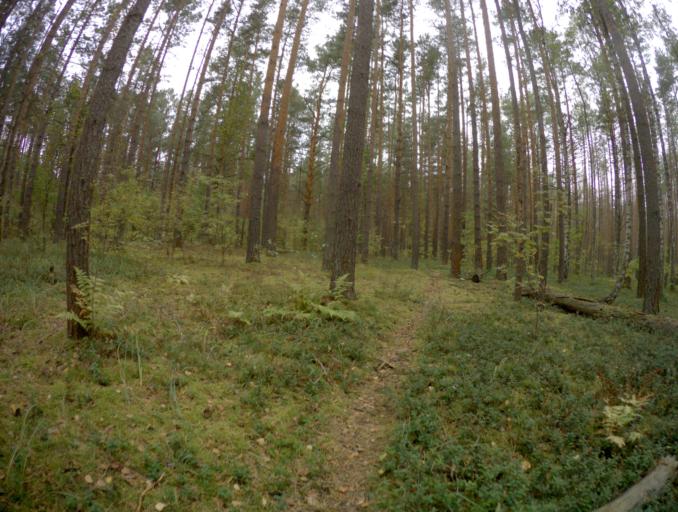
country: RU
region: Vladimir
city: Bogolyubovo
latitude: 56.1416
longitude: 40.5087
